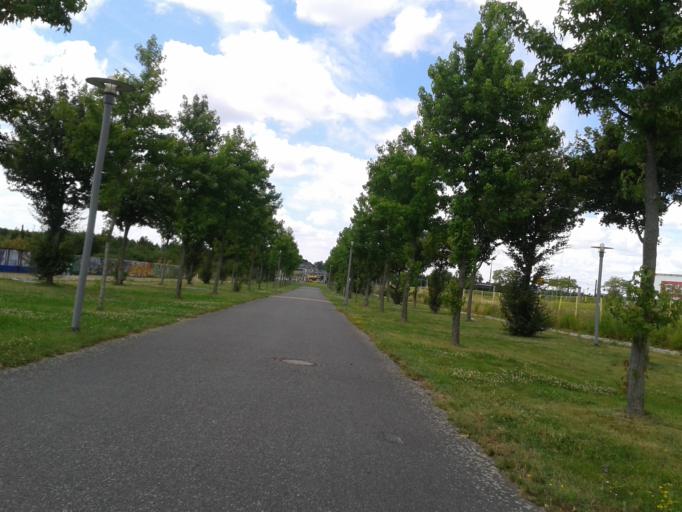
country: DE
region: Saxony
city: Radebeul
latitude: 51.0807
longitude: 13.6965
